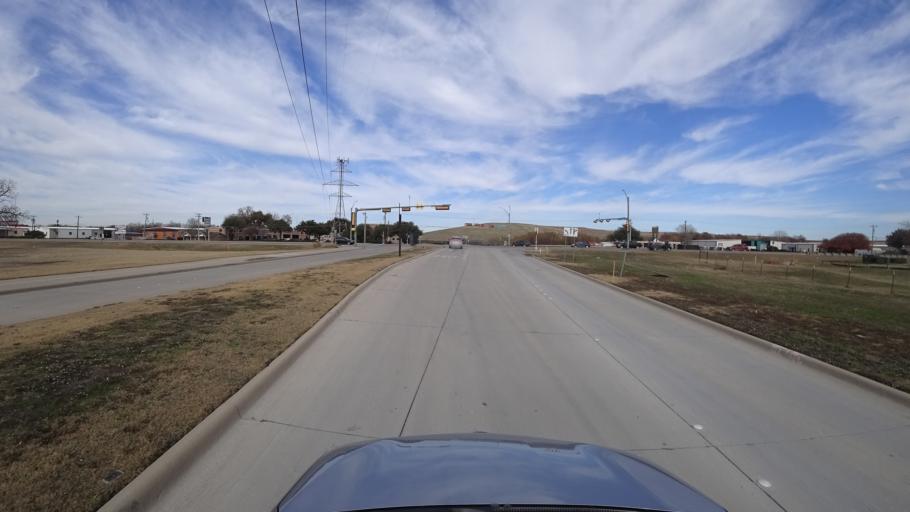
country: US
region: Texas
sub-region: Denton County
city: Lewisville
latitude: 33.0433
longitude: -96.9767
